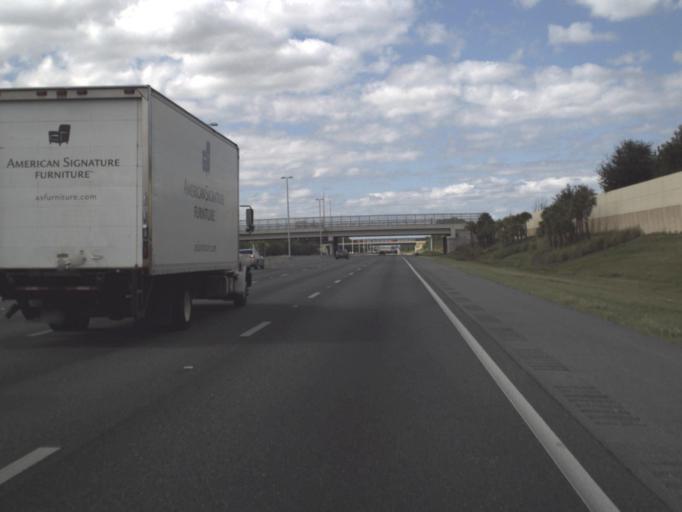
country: US
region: Florida
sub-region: Orange County
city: Winter Garden
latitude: 28.5454
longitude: -81.5807
